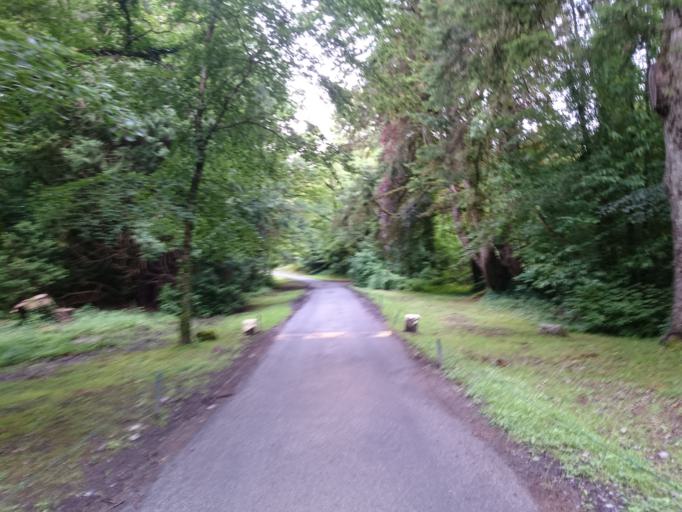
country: IE
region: Connaught
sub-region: Maigh Eo
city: Ballinrobe
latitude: 53.5355
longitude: -9.2884
